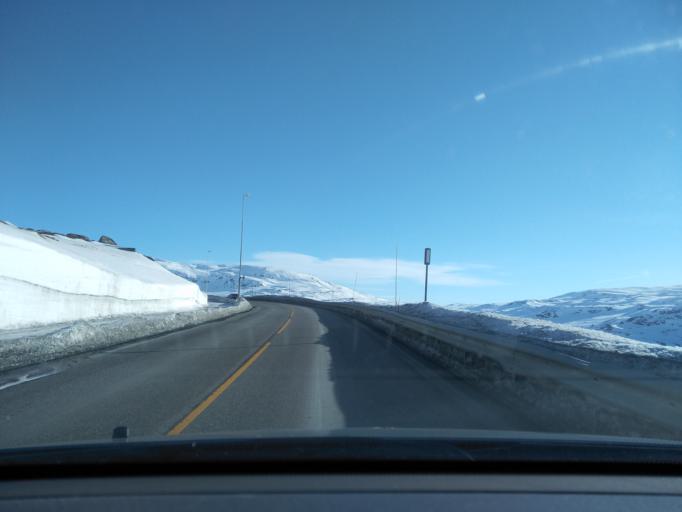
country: NO
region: Aust-Agder
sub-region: Bykle
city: Hovden
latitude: 59.8431
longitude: 6.9749
